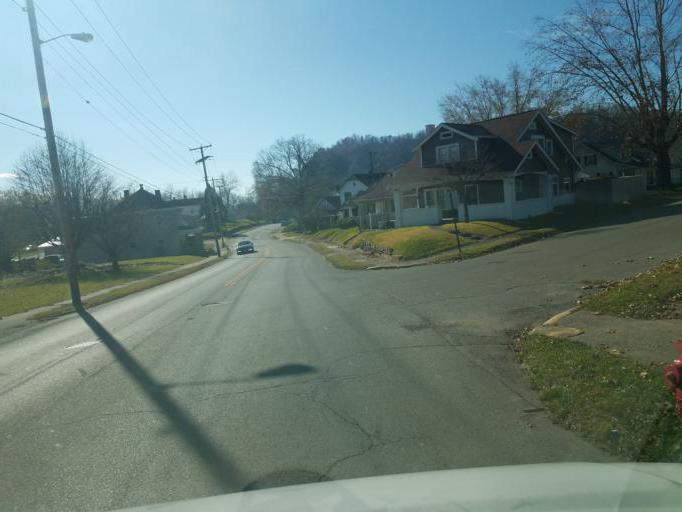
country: US
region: Ohio
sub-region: Scioto County
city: Sciotodale
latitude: 38.7654
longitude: -82.8893
